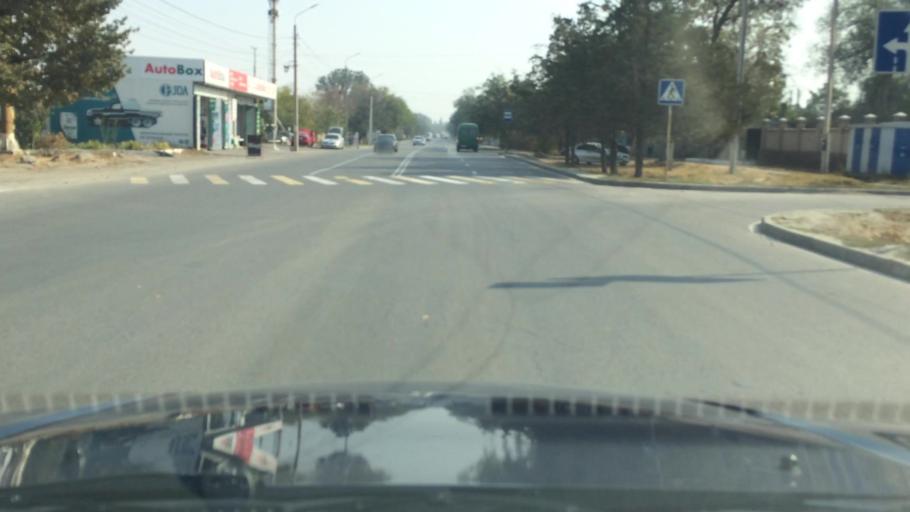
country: KG
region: Chuy
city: Lebedinovka
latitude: 42.8839
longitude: 74.6476
